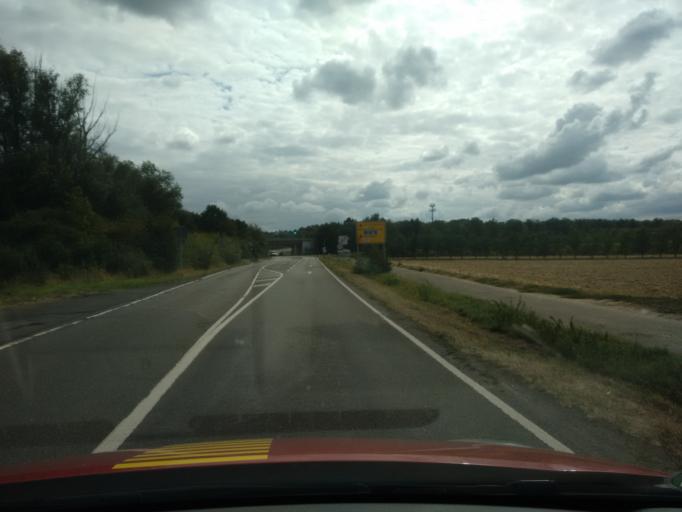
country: DE
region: Rheinland-Pfalz
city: Budenheim
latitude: 49.9913
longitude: 8.2052
